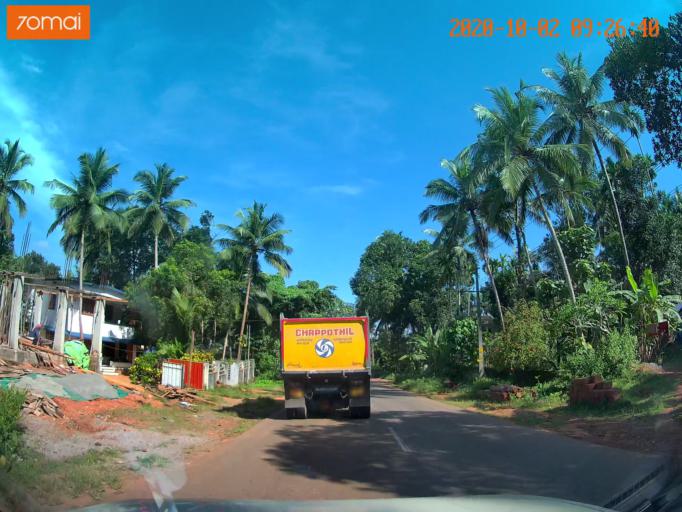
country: IN
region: Kerala
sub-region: Kozhikode
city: Naduvannur
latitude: 11.5938
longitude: 75.7660
